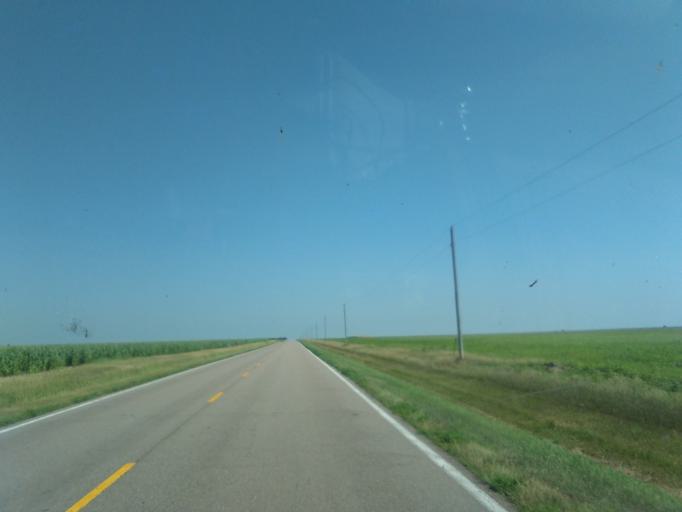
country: US
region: Nebraska
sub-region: Dundy County
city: Benkelman
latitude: 39.8323
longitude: -101.5411
